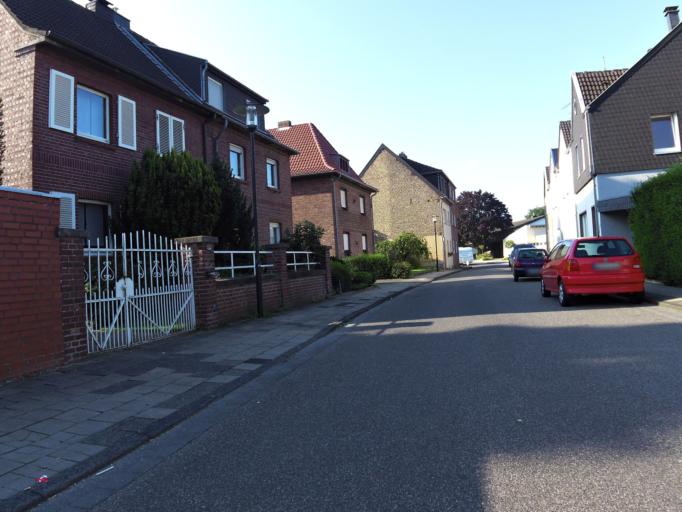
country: DE
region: North Rhine-Westphalia
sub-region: Regierungsbezirk Koln
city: Ubach-Palenberg
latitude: 50.9166
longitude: 6.1227
